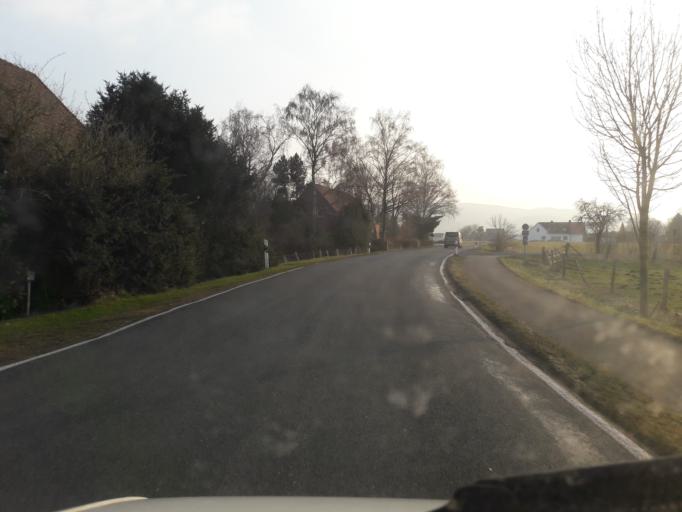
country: DE
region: North Rhine-Westphalia
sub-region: Regierungsbezirk Detmold
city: Huellhorst
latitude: 52.3269
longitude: 8.6676
